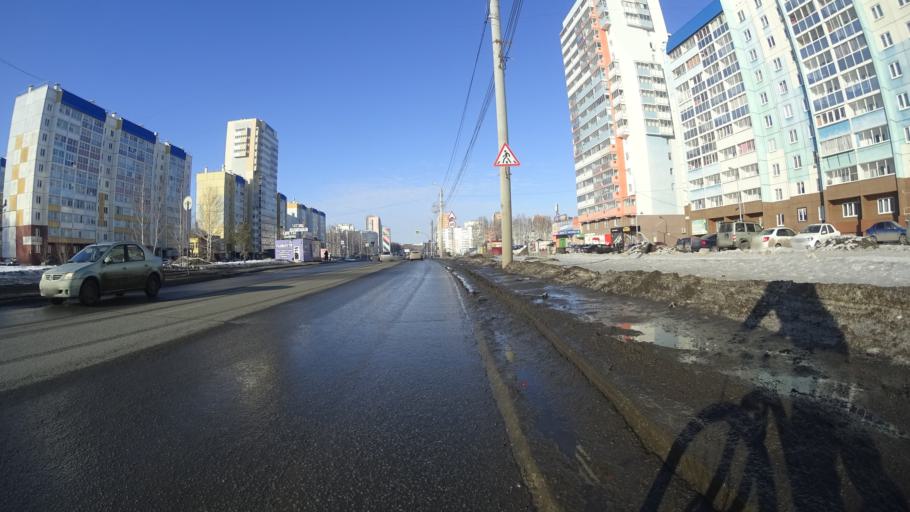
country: RU
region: Chelyabinsk
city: Roshchino
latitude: 55.2031
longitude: 61.2843
